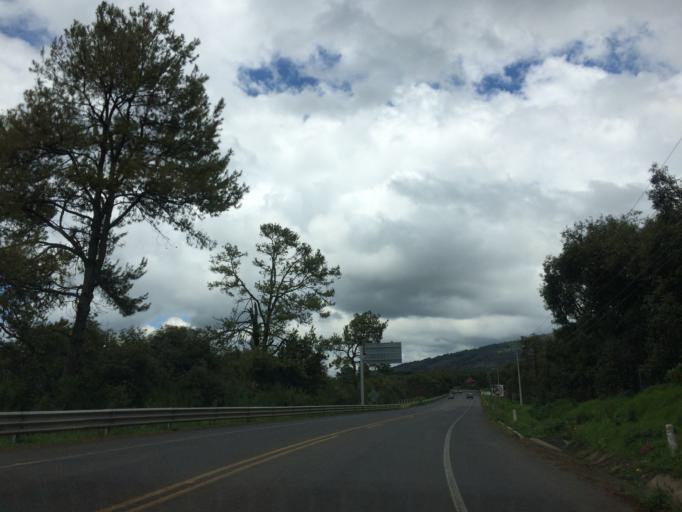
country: MX
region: Michoacan
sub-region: Uruapan
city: Santa Ana Zirosto
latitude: 19.5436
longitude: -102.3306
